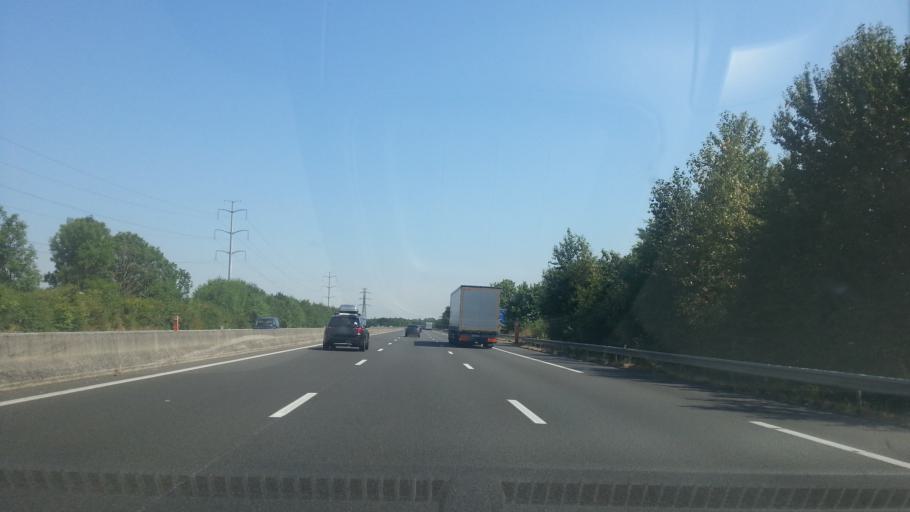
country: FR
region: Centre
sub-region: Departement du Loiret
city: Meung-sur-Loire
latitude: 47.8401
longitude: 1.6738
